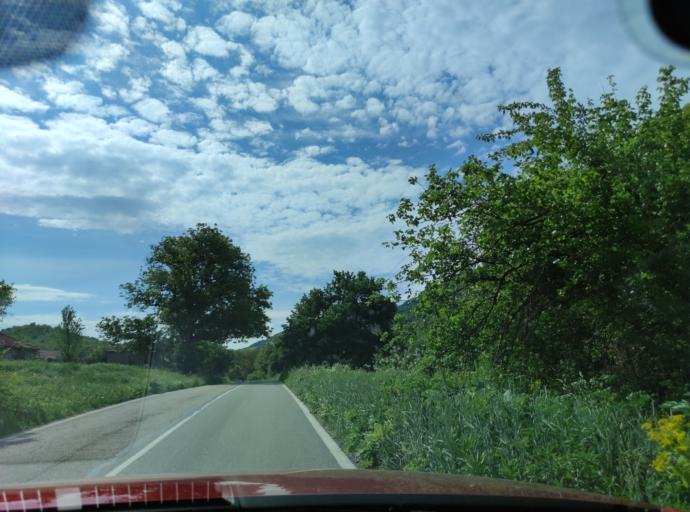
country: BG
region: Montana
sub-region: Obshtina Chiprovtsi
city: Chiprovtsi
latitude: 43.4900
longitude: 22.8101
